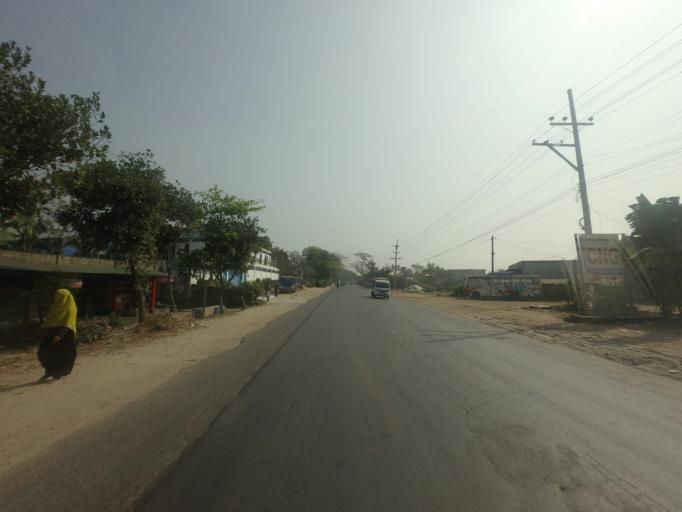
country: BD
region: Dhaka
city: Narsingdi
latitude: 23.8955
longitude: 90.6756
